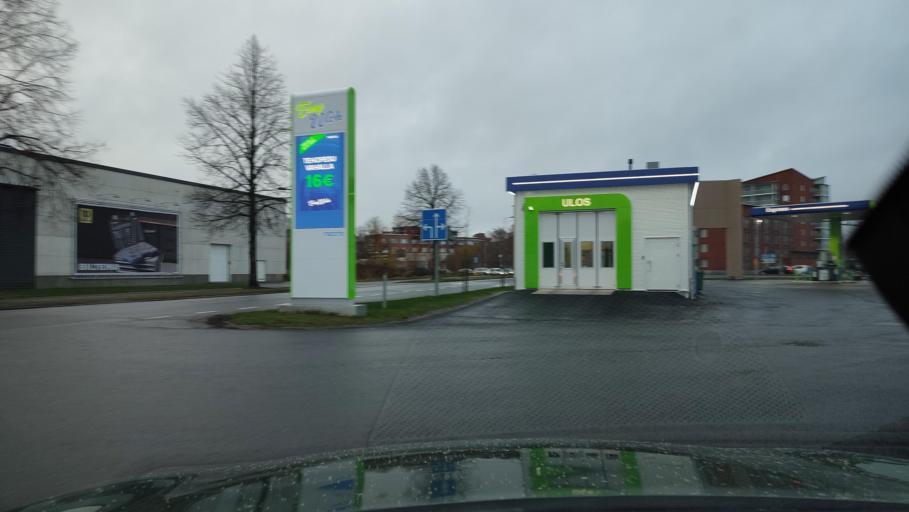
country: FI
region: Ostrobothnia
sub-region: Vaasa
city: Vaasa
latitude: 63.0990
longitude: 21.6346
